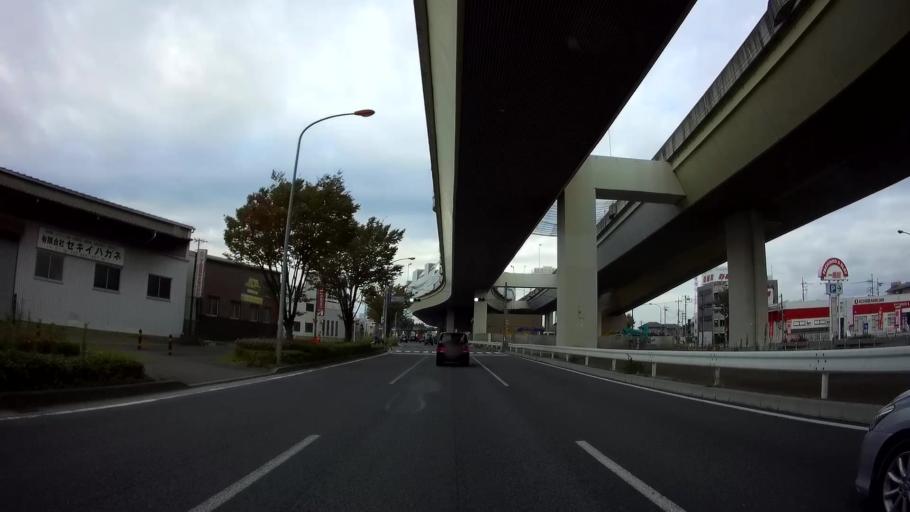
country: JP
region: Saitama
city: Asaka
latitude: 35.8318
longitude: 139.6339
